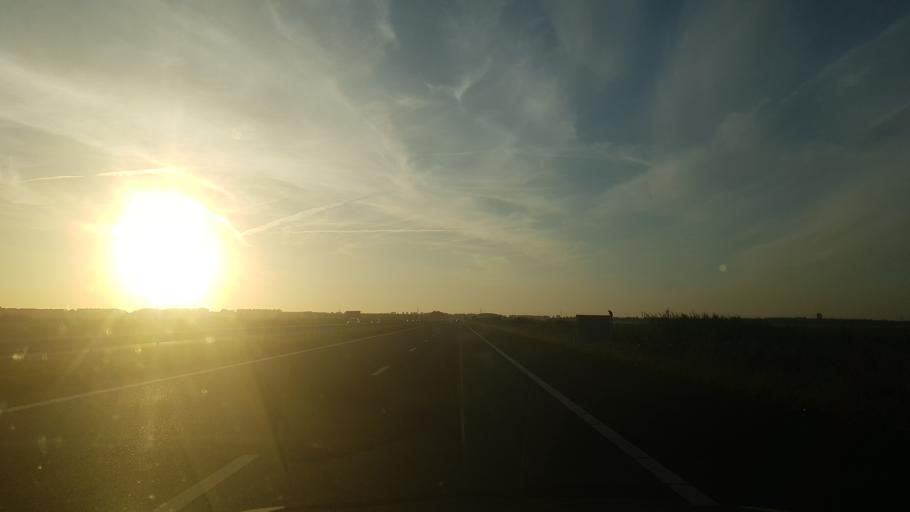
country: NL
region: North Holland
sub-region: Gemeente Huizen
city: Huizen
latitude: 52.3620
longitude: 5.3234
